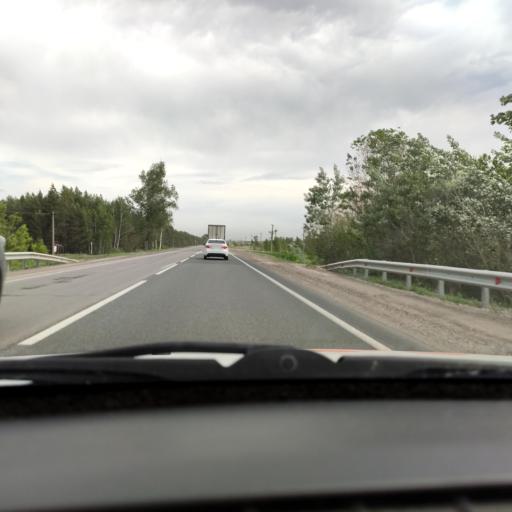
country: RU
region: Samara
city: Mirnyy
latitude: 53.5097
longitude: 50.3047
